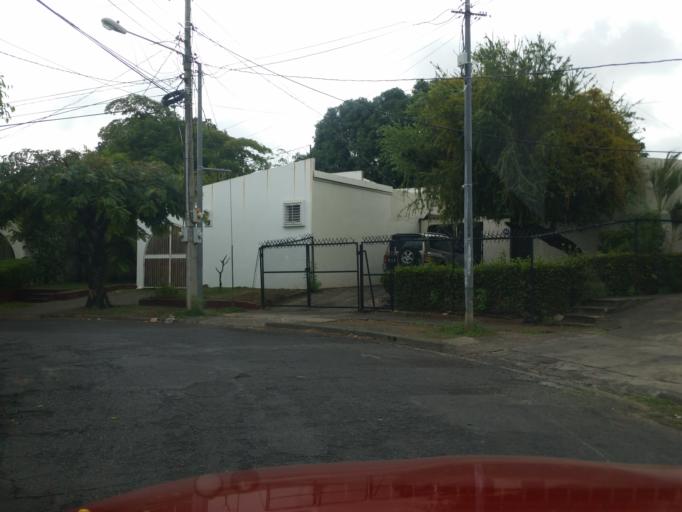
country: NI
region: Managua
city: Managua
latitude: 12.1052
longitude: -86.2637
